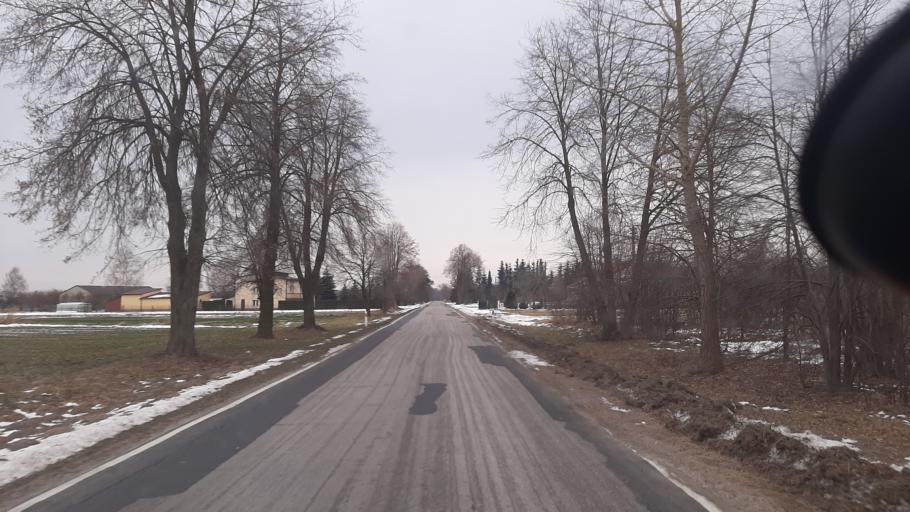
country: PL
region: Lublin Voivodeship
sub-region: Powiat lubartowski
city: Kamionka
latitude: 51.4590
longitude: 22.4207
